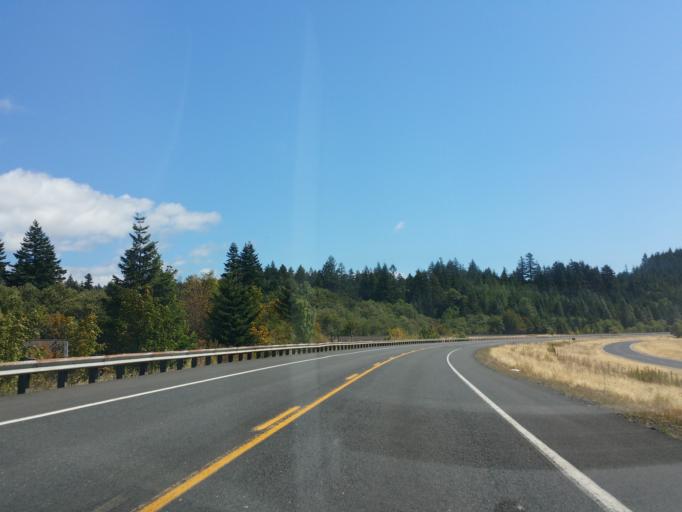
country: US
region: Oregon
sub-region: Hood River County
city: Cascade Locks
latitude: 45.6513
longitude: -121.9449
